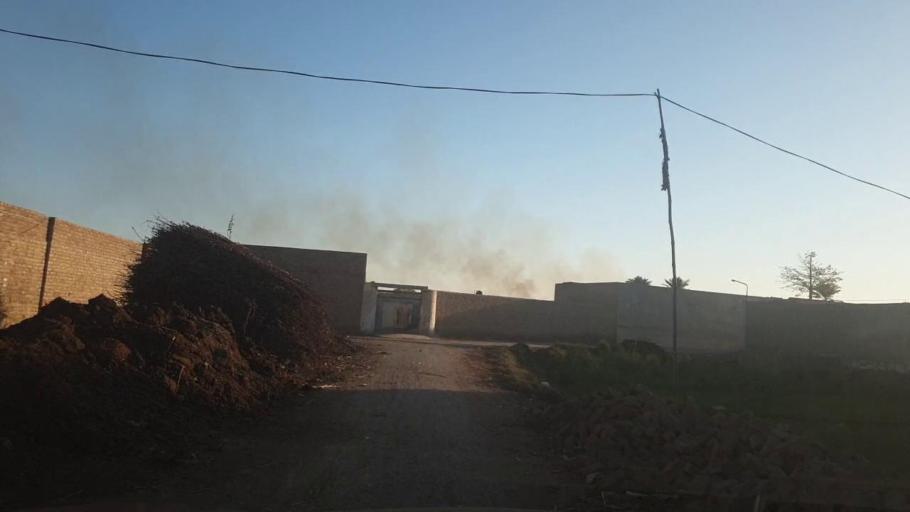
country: PK
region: Sindh
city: Ghotki
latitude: 27.9945
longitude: 69.2832
